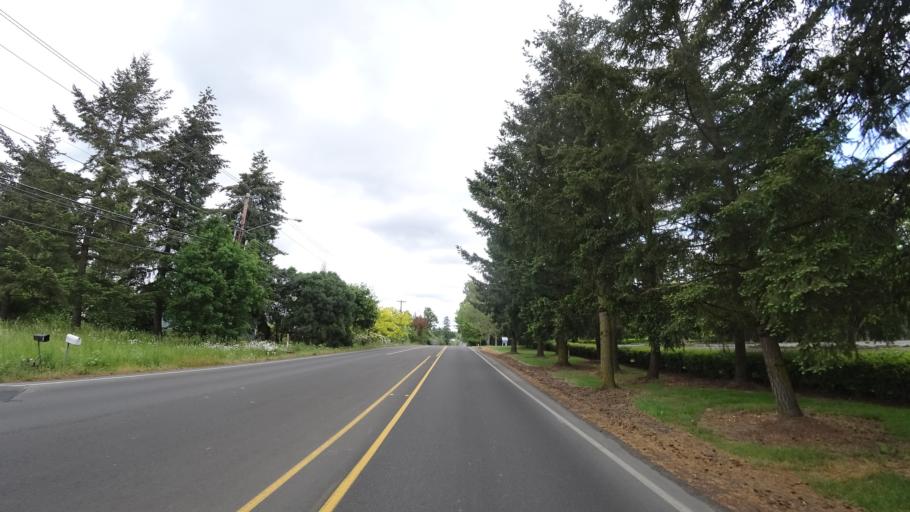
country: US
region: Oregon
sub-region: Washington County
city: Rockcreek
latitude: 45.5316
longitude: -122.8774
